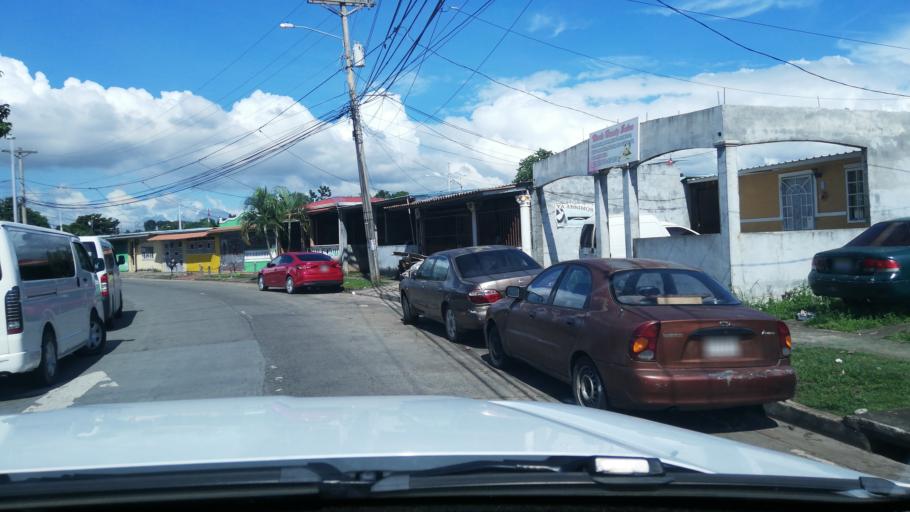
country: PA
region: Panama
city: Tocumen
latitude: 9.0805
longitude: -79.3566
